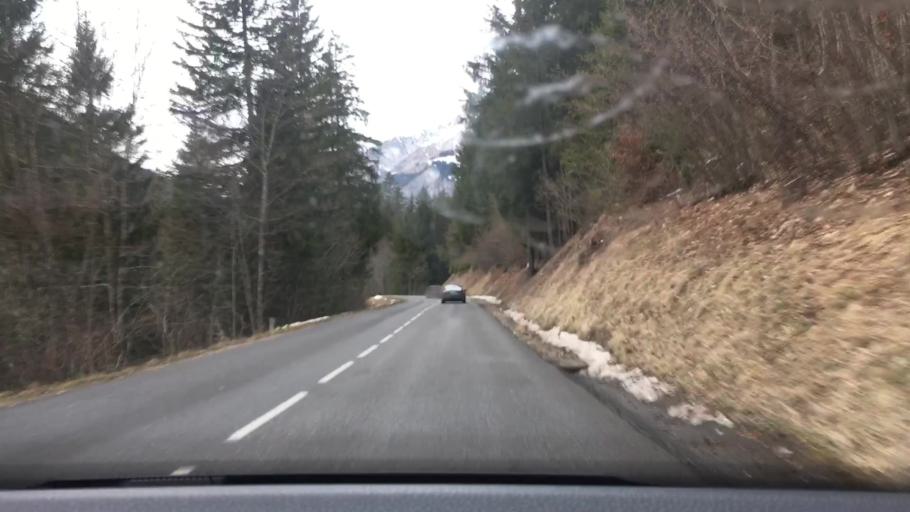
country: FR
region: Rhone-Alpes
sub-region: Departement de la Haute-Savoie
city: Chatel
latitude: 46.2818
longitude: 6.8214
